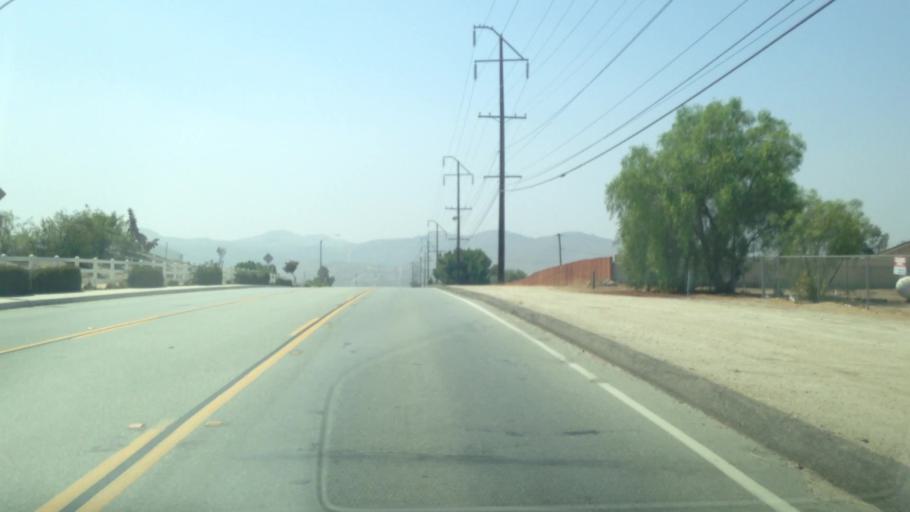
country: US
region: California
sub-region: Riverside County
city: Mead Valley
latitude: 33.8500
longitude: -117.3313
